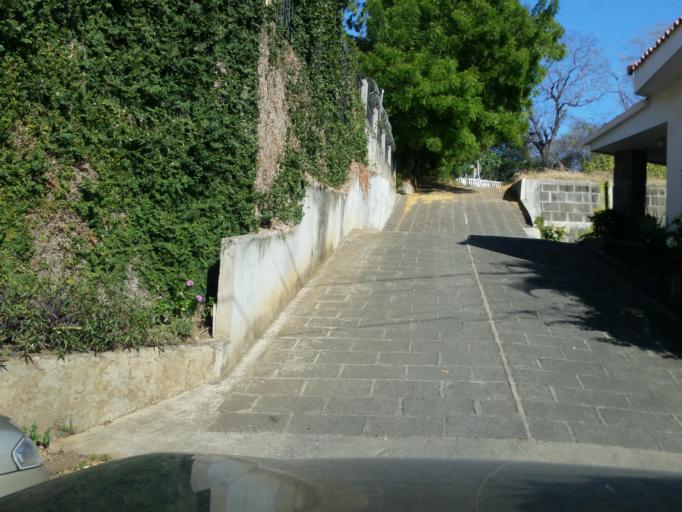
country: NI
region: Managua
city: Managua
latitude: 12.0975
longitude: -86.2375
